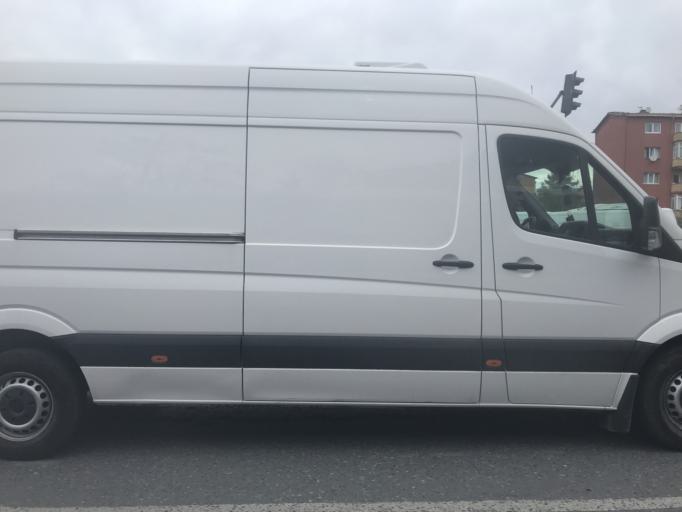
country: TR
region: Istanbul
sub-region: Atasehir
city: Atasehir
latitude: 40.9896
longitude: 29.1474
